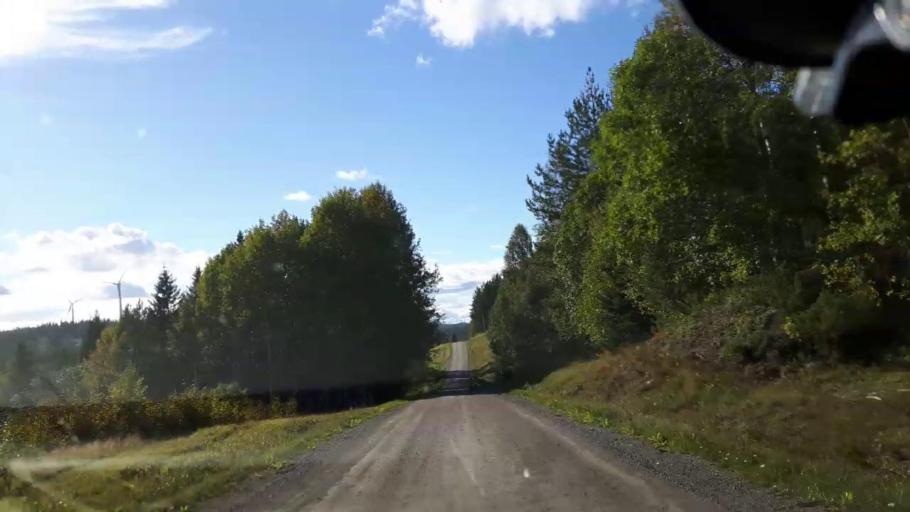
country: SE
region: Jaemtland
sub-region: Ragunda Kommun
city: Hammarstrand
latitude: 63.4758
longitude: 16.1632
